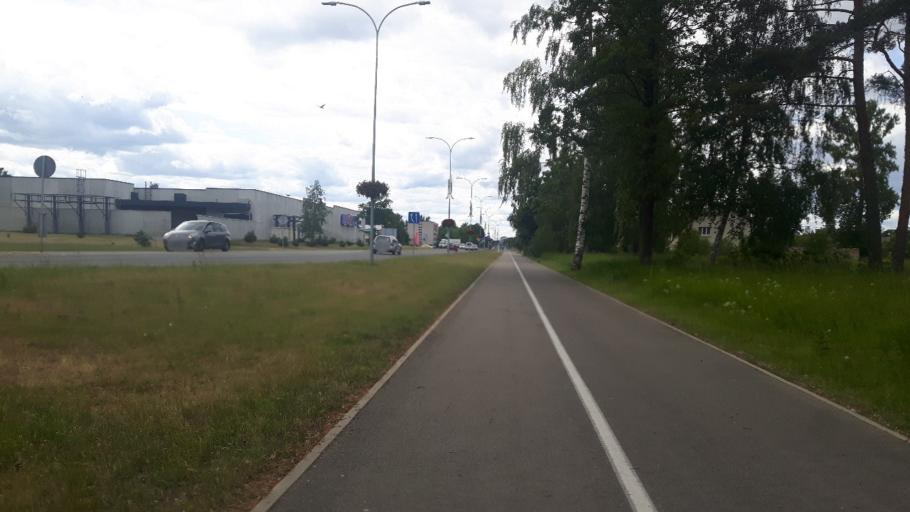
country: LV
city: Tireli
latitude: 56.9603
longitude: 23.6203
